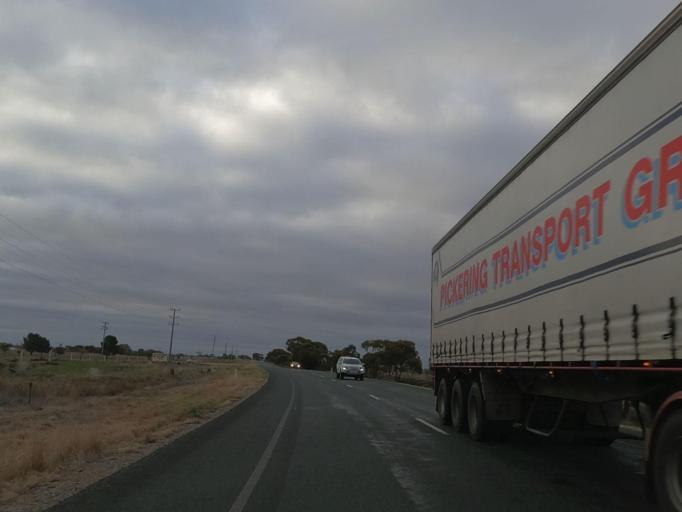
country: AU
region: Victoria
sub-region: Swan Hill
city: Swan Hill
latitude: -35.5840
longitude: 143.7901
